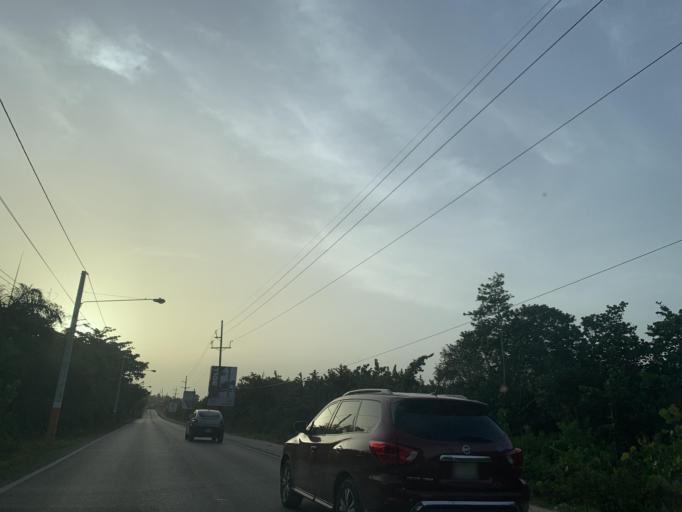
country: DO
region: Puerto Plata
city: Cabarete
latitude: 19.7704
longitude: -70.4367
